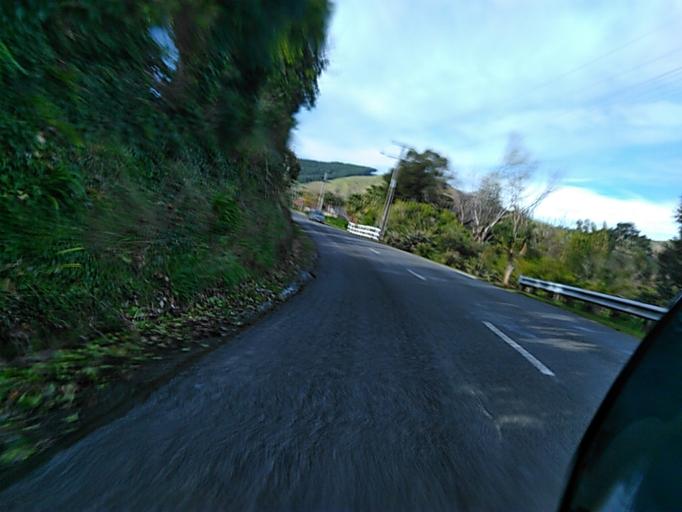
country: NZ
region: Gisborne
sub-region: Gisborne District
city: Gisborne
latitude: -38.6638
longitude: 178.0457
